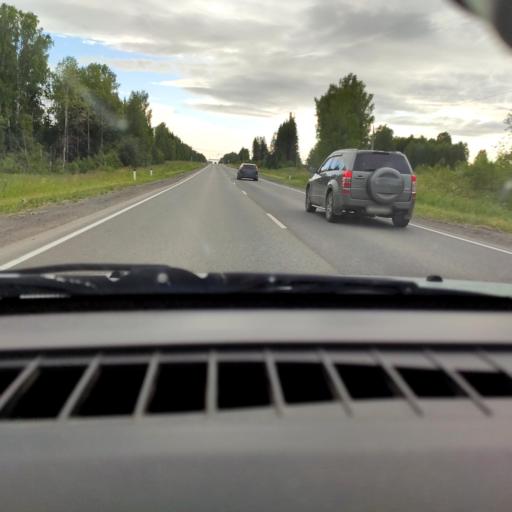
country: RU
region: Perm
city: Orda
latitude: 57.2543
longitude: 57.0033
